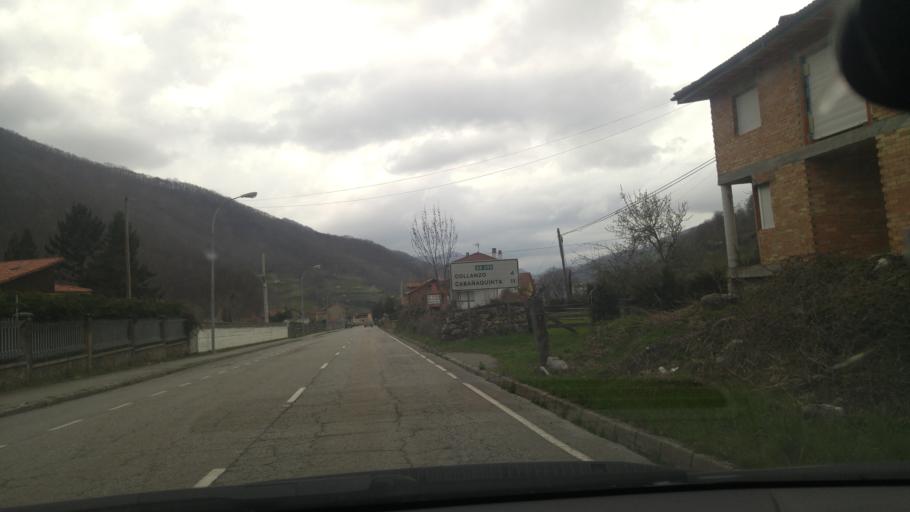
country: ES
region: Asturias
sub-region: Province of Asturias
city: Rio Aller
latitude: 43.1065
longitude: -5.5163
